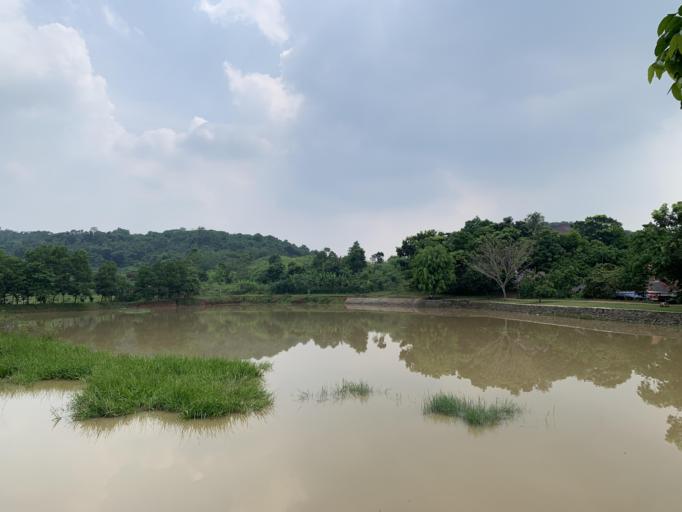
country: ID
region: West Java
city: Serpong
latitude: -6.3795
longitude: 106.5861
